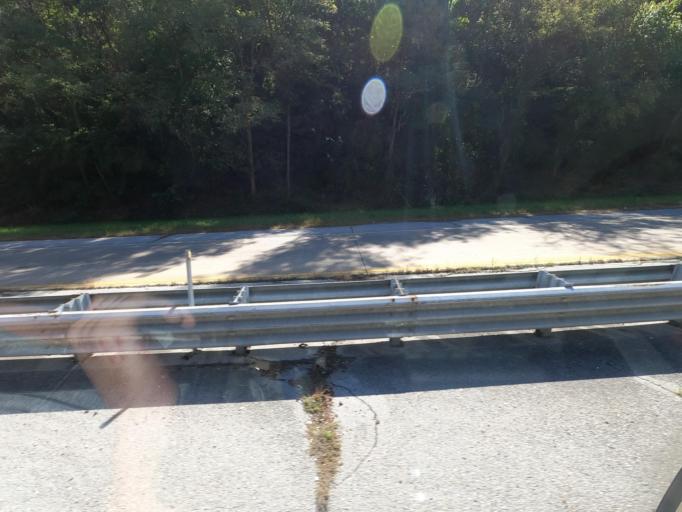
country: US
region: Tennessee
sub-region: Hamblen County
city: Morristown
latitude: 36.1931
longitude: -83.2685
